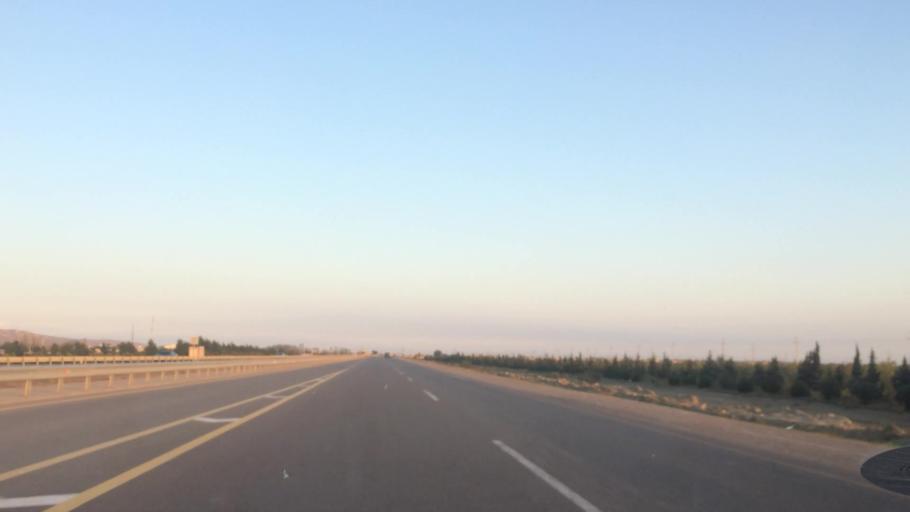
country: AZ
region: Baki
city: Qobustan
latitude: 39.9778
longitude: 49.2438
